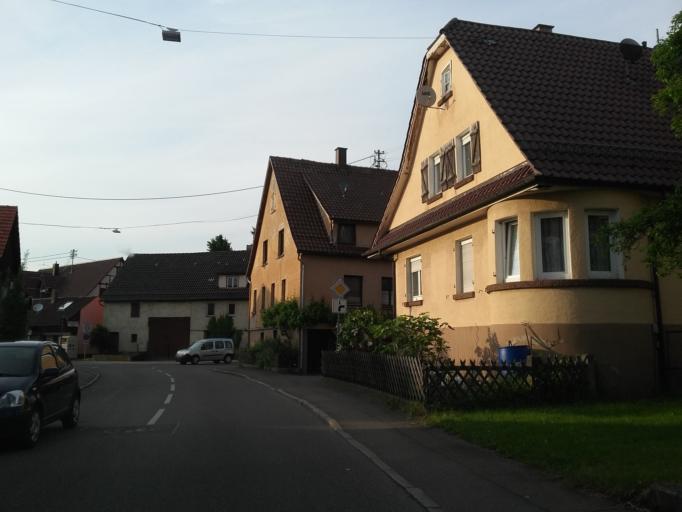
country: DE
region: Baden-Wuerttemberg
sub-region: Regierungsbezirk Stuttgart
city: Leutenbach
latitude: 48.9022
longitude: 9.4051
